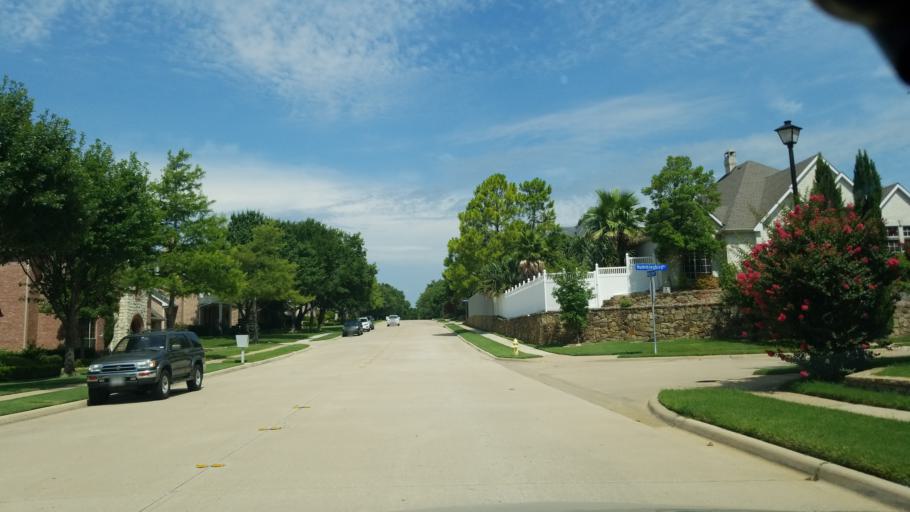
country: US
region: Texas
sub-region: Dallas County
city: Coppell
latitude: 32.9579
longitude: -96.9616
